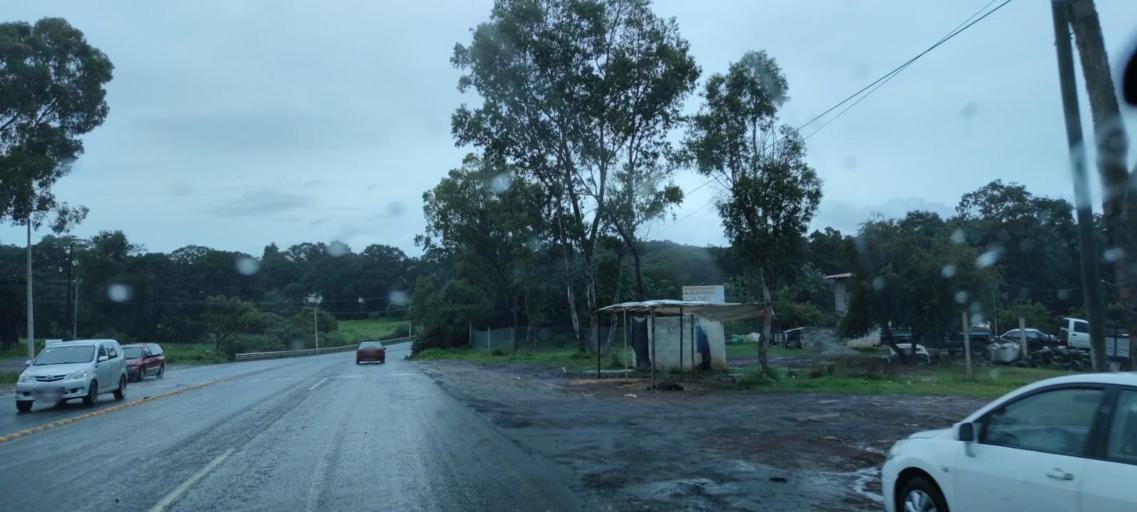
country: MX
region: Mexico
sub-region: Jilotepec
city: Doxhicho
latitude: 19.9366
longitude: -99.5667
